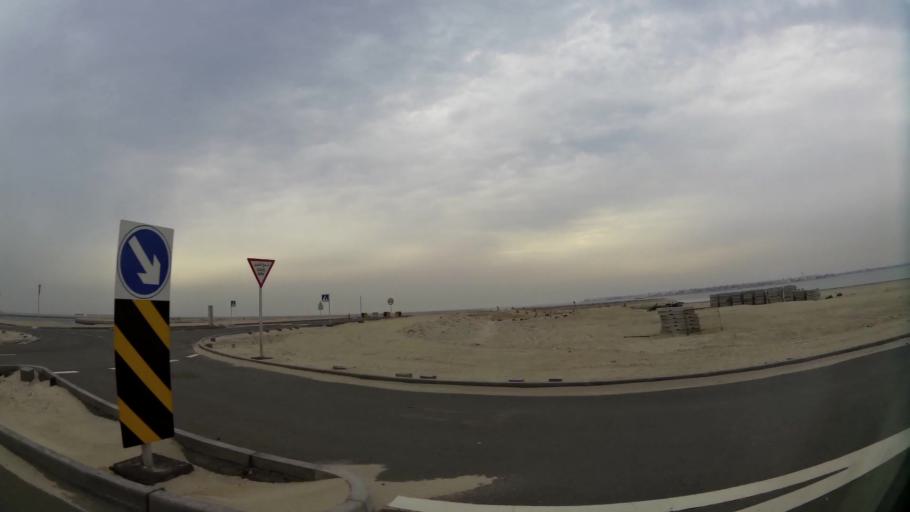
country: BH
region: Central Governorate
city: Dar Kulayb
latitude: 25.8623
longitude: 50.6067
